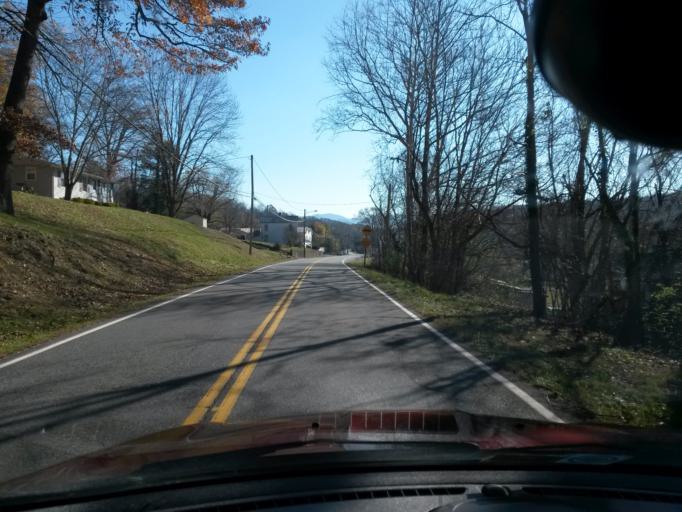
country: US
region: Virginia
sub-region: Botetourt County
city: Fincastle
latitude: 37.6414
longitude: -79.8028
